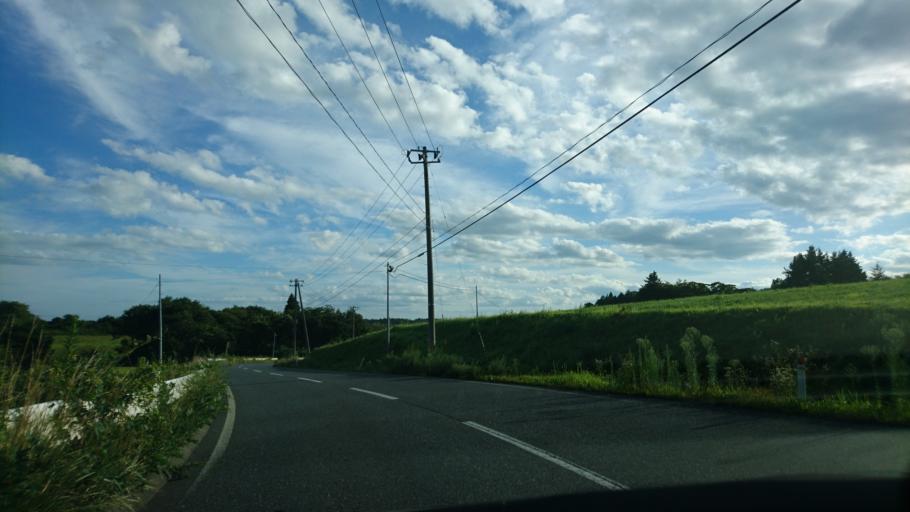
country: JP
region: Iwate
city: Ichinoseki
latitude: 38.8772
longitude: 141.1990
